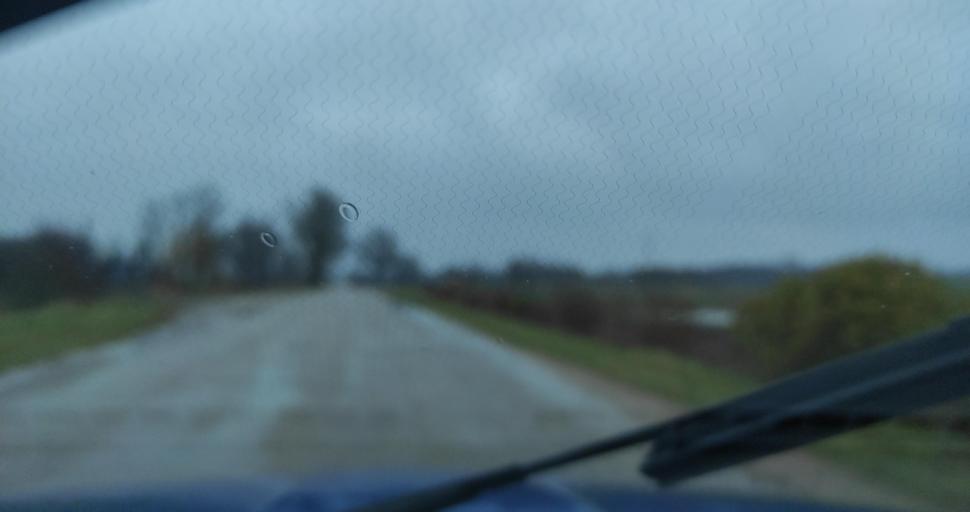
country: LV
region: Alsunga
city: Alsunga
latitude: 56.9021
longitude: 21.6197
